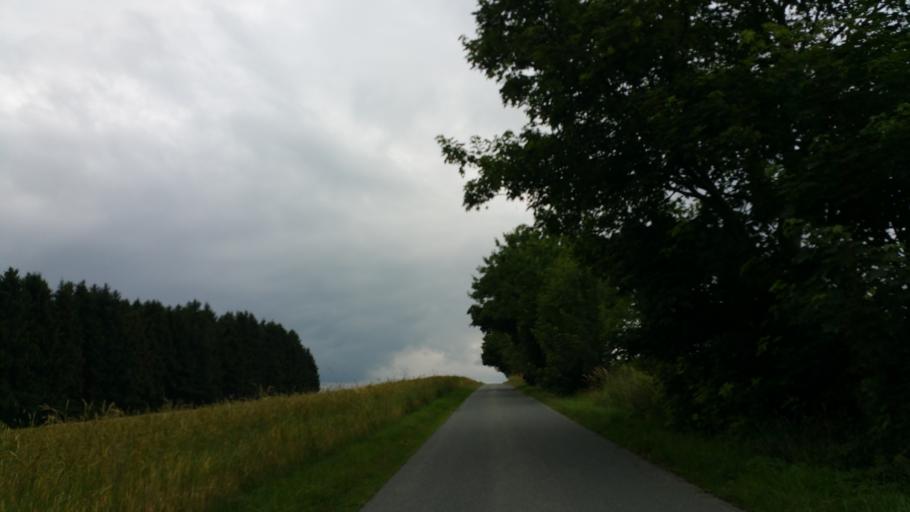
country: DE
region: Bavaria
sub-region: Upper Franconia
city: Oberkotzau
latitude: 50.2431
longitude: 11.9190
